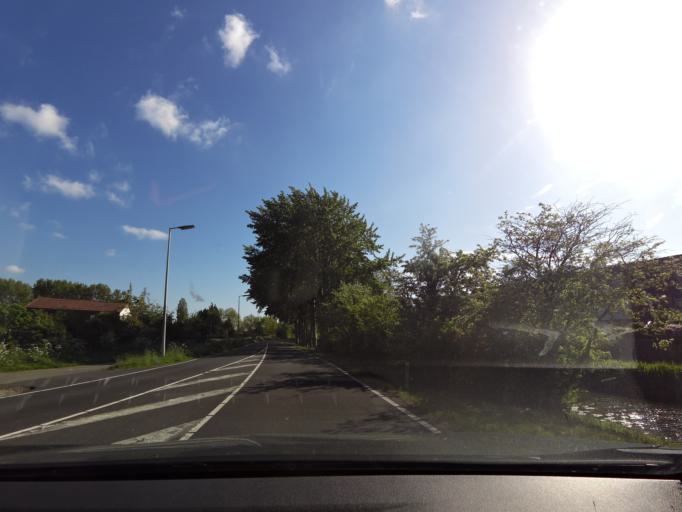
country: NL
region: South Holland
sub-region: Gemeente Hellevoetsluis
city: Nieuw-Helvoet
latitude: 51.8692
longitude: 4.0762
